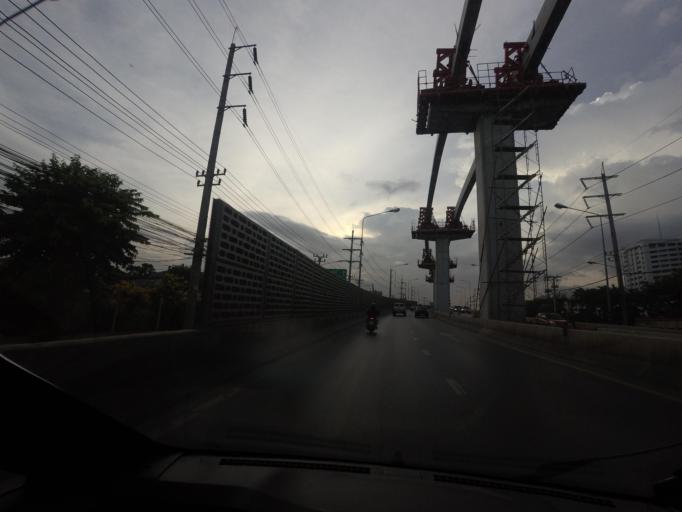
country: TH
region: Bangkok
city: Khan Na Yao
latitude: 13.8131
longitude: 100.6889
